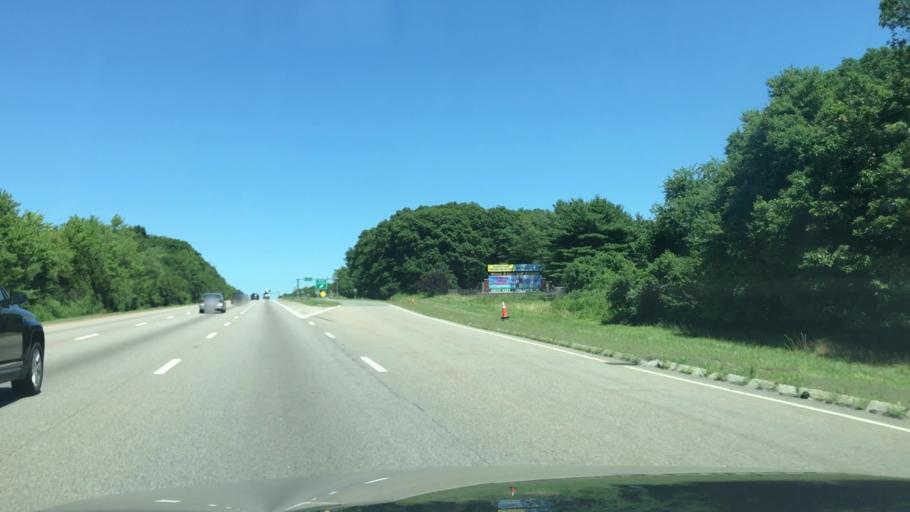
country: US
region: Massachusetts
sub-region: Bristol County
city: North Seekonk
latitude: 41.9138
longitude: -71.3351
